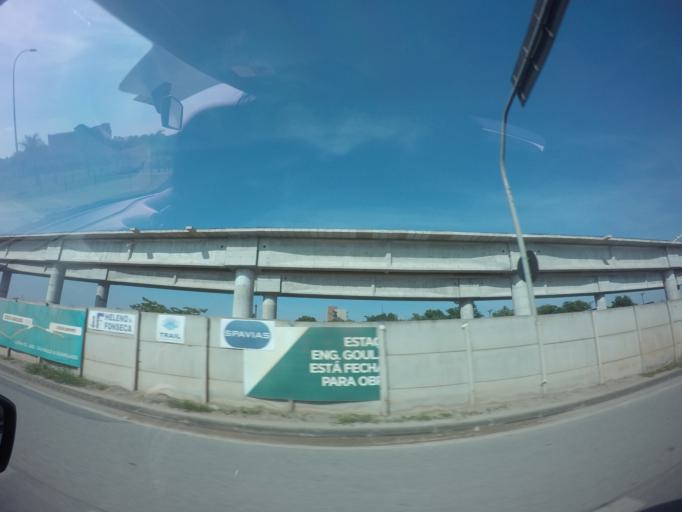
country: BR
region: Sao Paulo
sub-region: Guarulhos
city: Guarulhos
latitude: -23.4486
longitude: -46.4929
